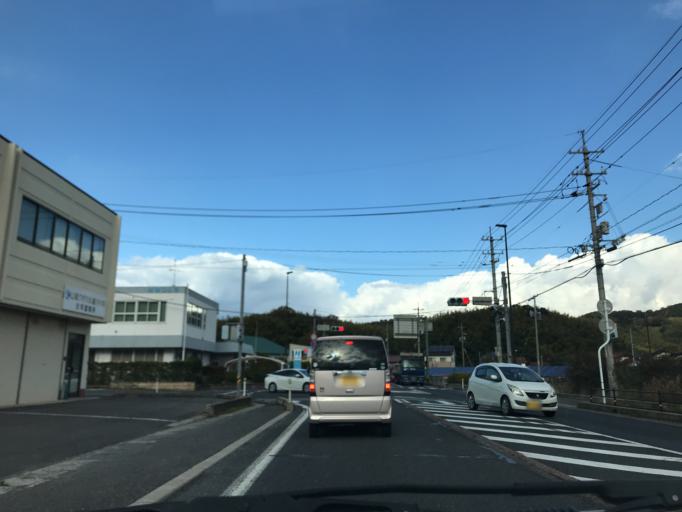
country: JP
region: Tottori
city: Yonago
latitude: 35.4154
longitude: 133.2917
